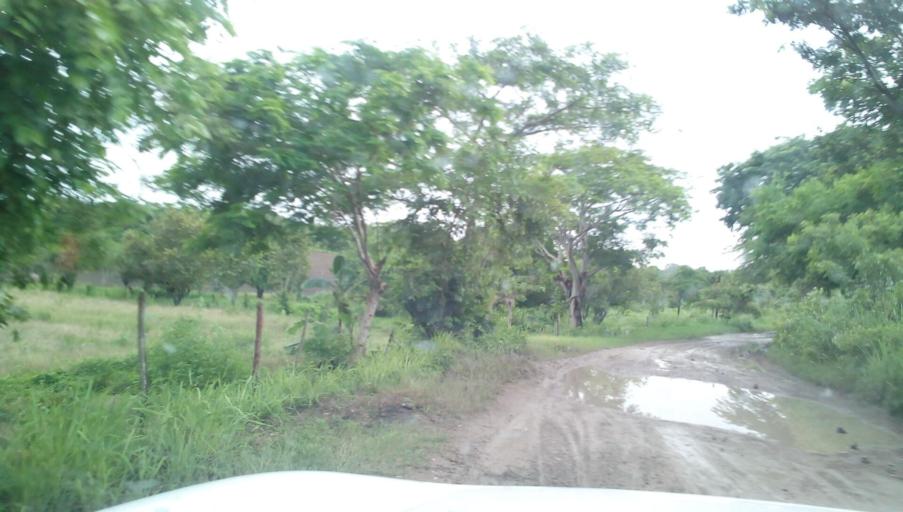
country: MX
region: Veracruz
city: Panuco
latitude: 21.8071
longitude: -98.1057
